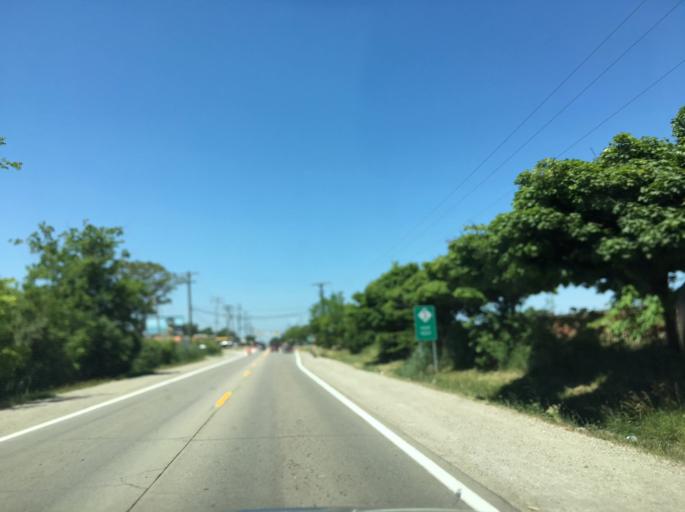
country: US
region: Michigan
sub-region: Macomb County
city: Fraser
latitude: 42.5398
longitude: -82.9060
